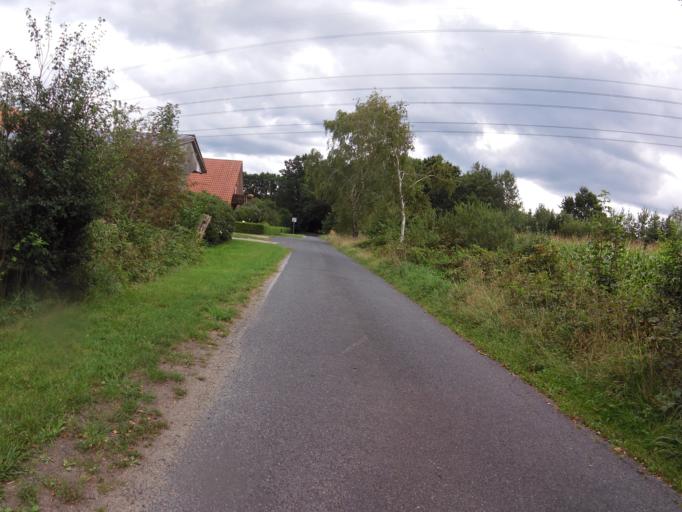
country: DE
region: Lower Saxony
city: Kohlen
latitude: 53.5068
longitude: 8.8794
